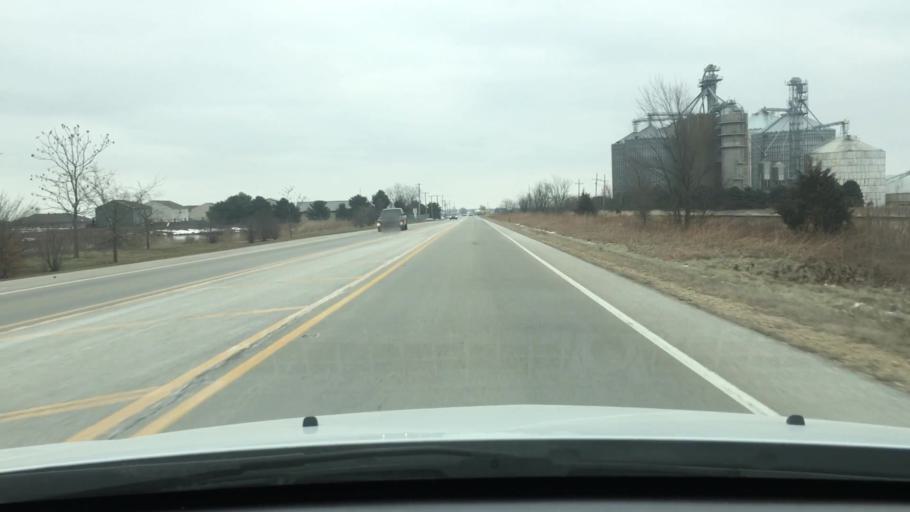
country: US
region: Illinois
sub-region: DeKalb County
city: Waterman
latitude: 41.7691
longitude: -88.7620
